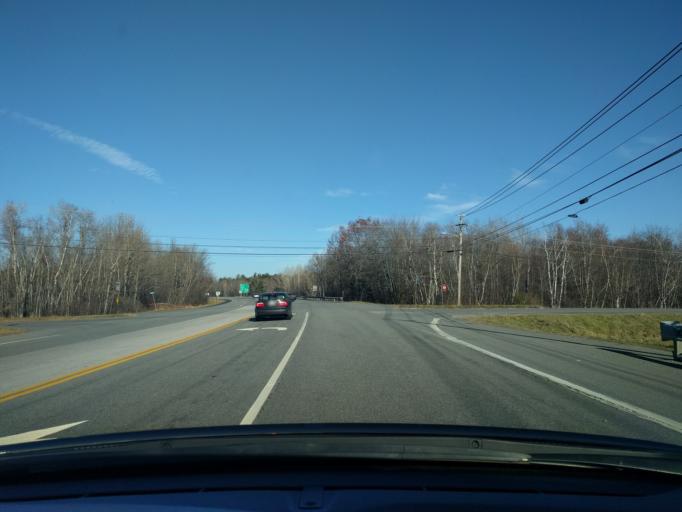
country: US
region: Maine
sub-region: Penobscot County
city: Bangor
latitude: 44.7786
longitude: -68.7974
